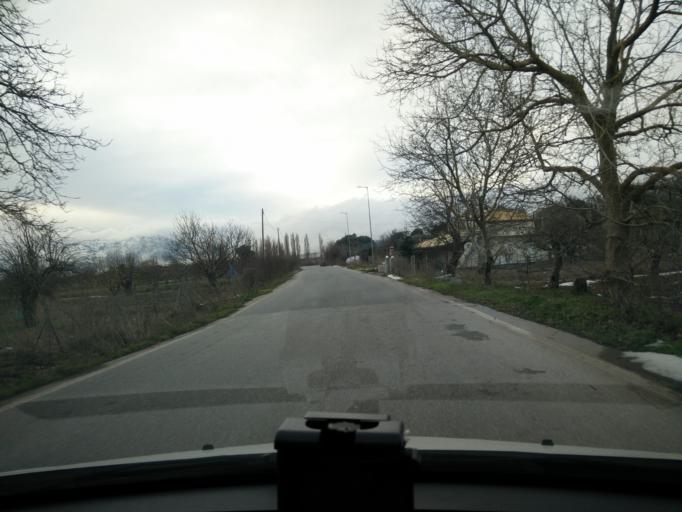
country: GR
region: Crete
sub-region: Nomos Irakleiou
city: Malia
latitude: 35.1916
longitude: 25.4938
